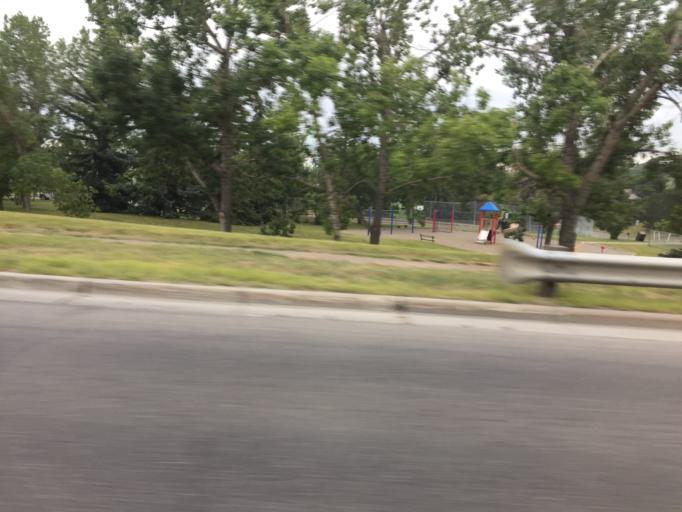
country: CA
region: Alberta
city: Calgary
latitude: 51.0247
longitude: -114.1240
